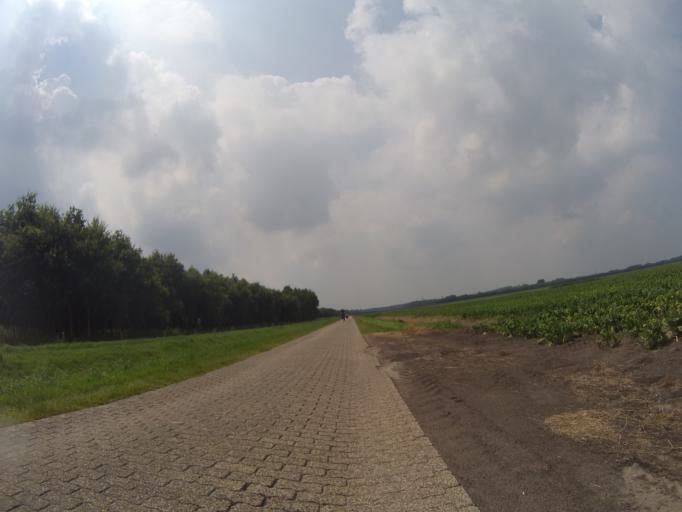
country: NL
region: Drenthe
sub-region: Gemeente Emmen
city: Klazienaveen
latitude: 52.7848
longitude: 6.9843
